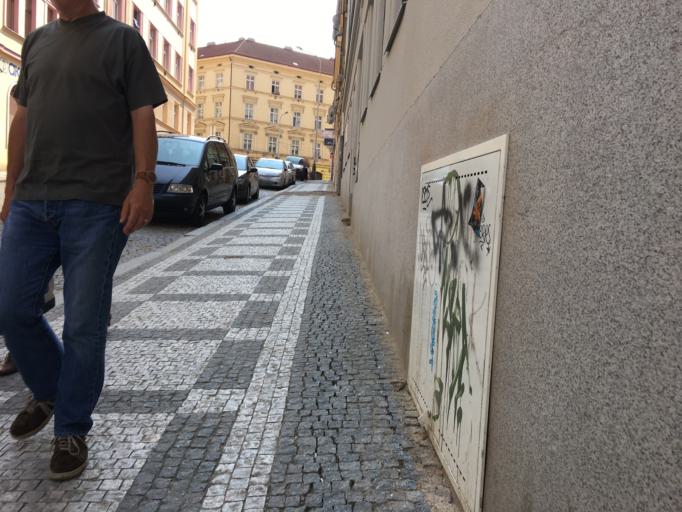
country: CZ
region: Praha
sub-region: Praha 8
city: Karlin
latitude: 50.0852
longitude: 14.4494
